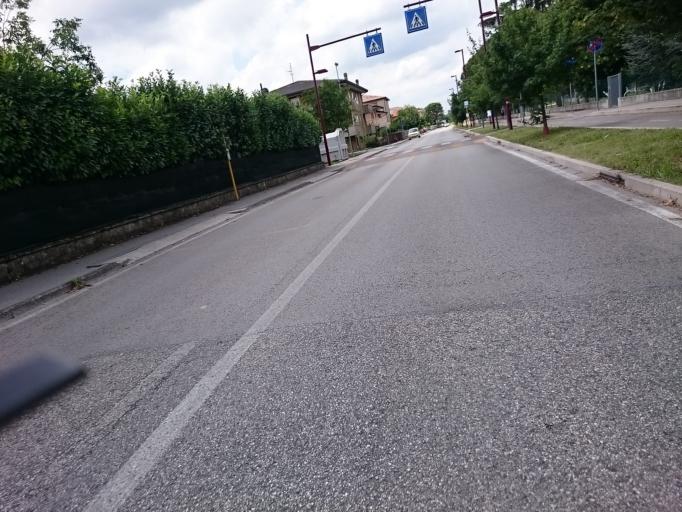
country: IT
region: Veneto
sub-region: Provincia di Padova
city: Sarmeola
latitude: 45.4263
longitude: 11.8107
